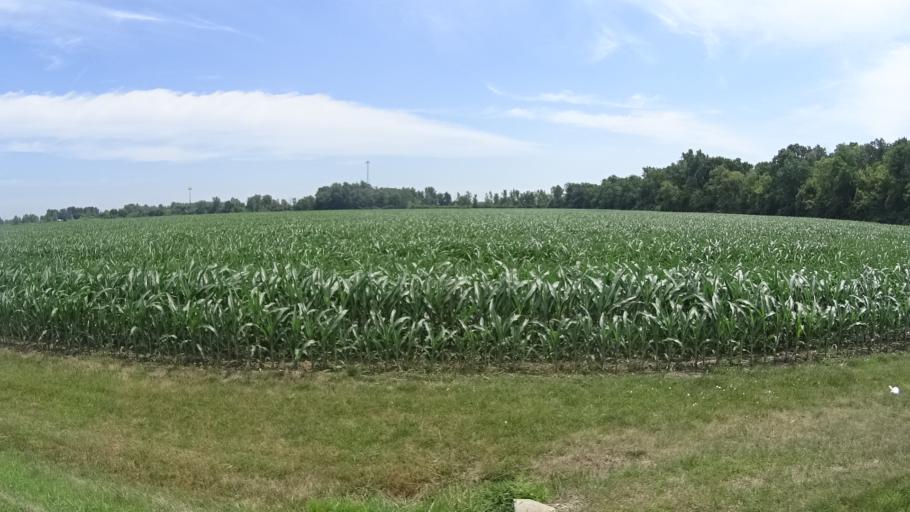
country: US
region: Ohio
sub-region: Erie County
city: Sandusky
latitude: 41.4279
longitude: -82.7625
